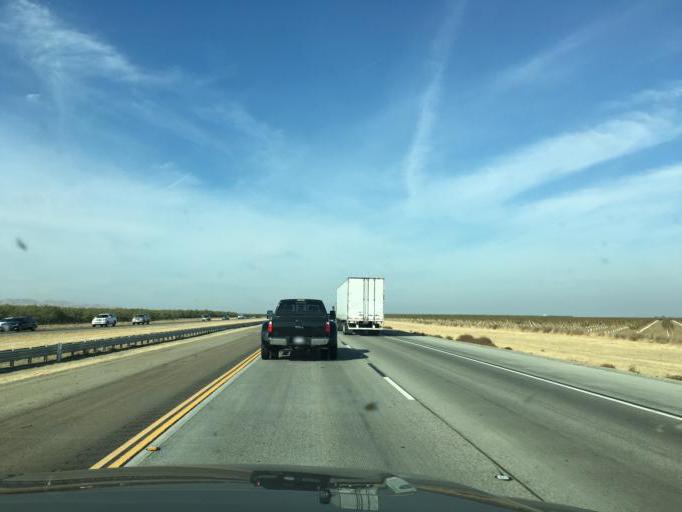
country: US
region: California
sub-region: Fresno County
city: Firebaugh
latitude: 36.6581
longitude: -120.6368
